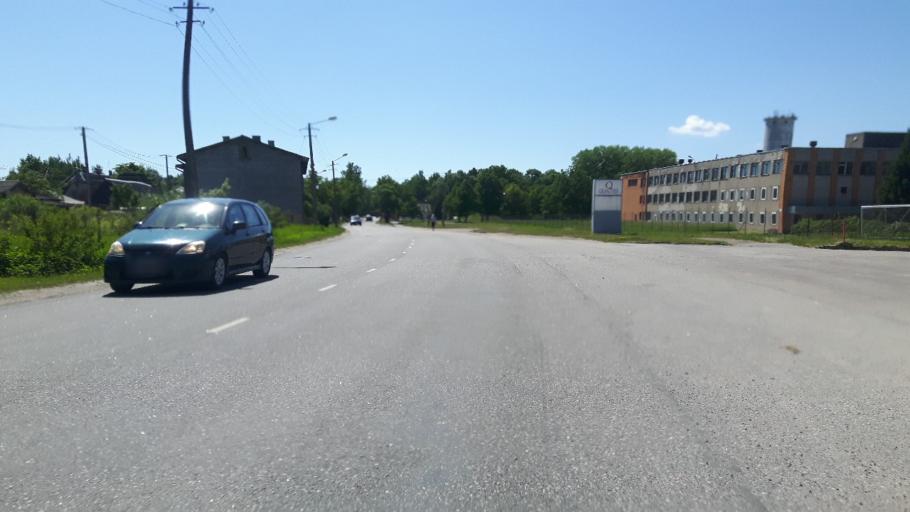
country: EE
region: Paernumaa
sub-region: Sindi linn
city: Sindi
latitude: 58.4100
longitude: 24.6634
